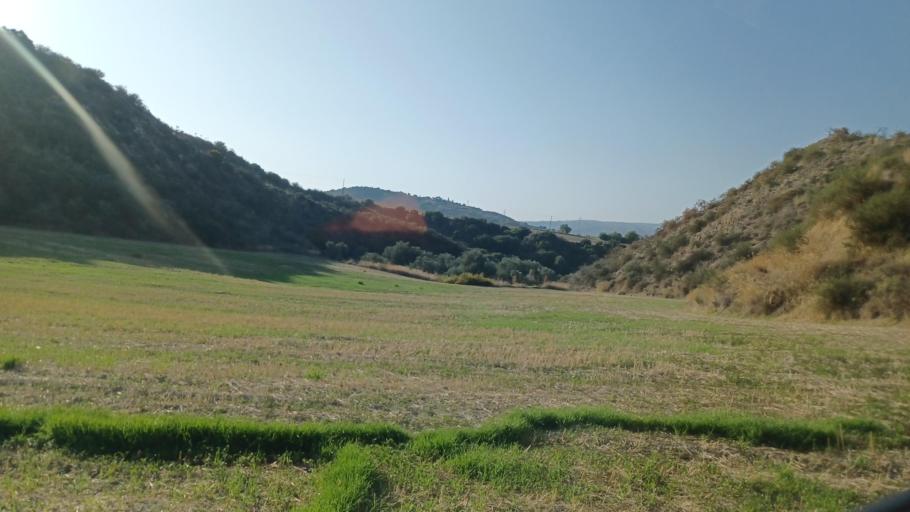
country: CY
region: Pafos
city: Polis
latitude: 35.0027
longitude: 32.4570
